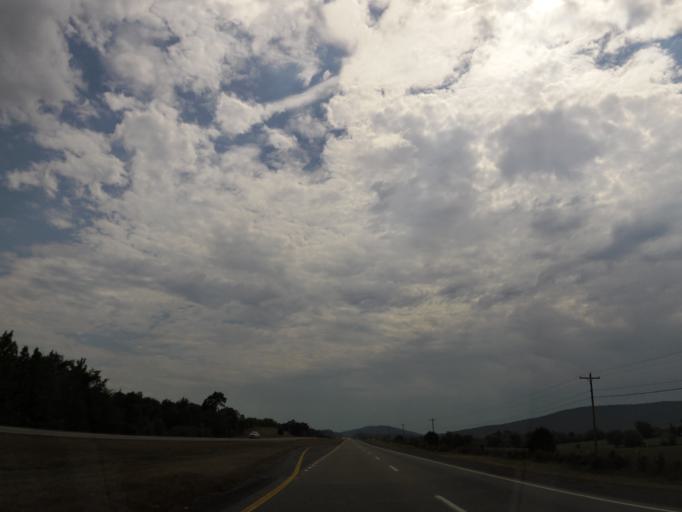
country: US
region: Alabama
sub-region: Jackson County
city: Bridgeport
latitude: 34.9324
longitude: -85.7638
